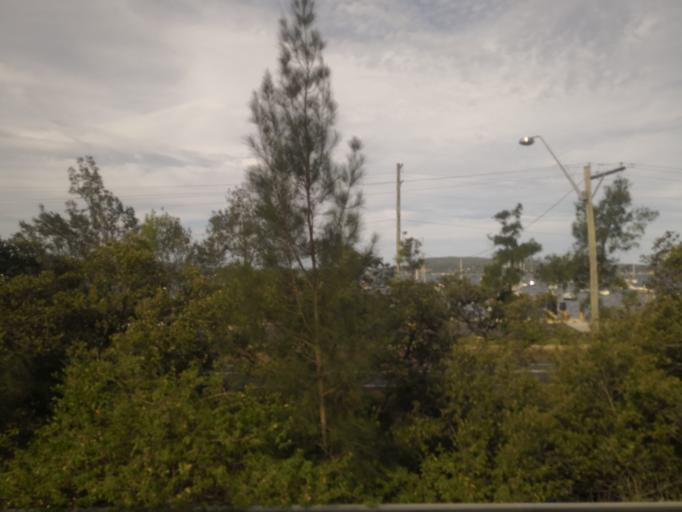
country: AU
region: New South Wales
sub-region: Gosford Shire
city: Point Clare
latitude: -33.4613
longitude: 151.3130
